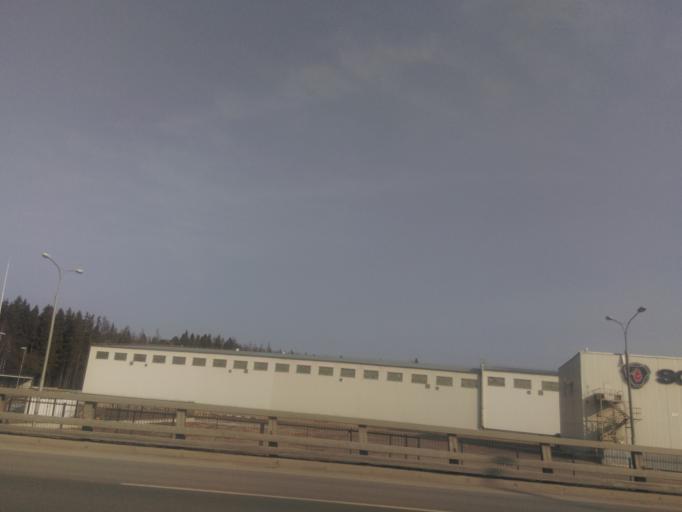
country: RU
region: Moskovskaya
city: Krasnoznamensk
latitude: 55.6053
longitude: 37.0205
